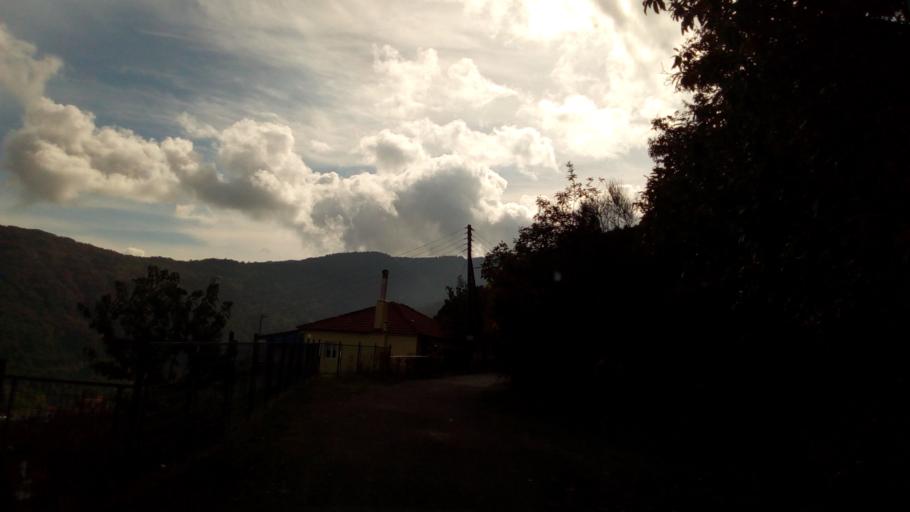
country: GR
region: Central Greece
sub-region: Nomos Fokidos
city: Lidoriki
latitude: 38.4908
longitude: 22.0513
